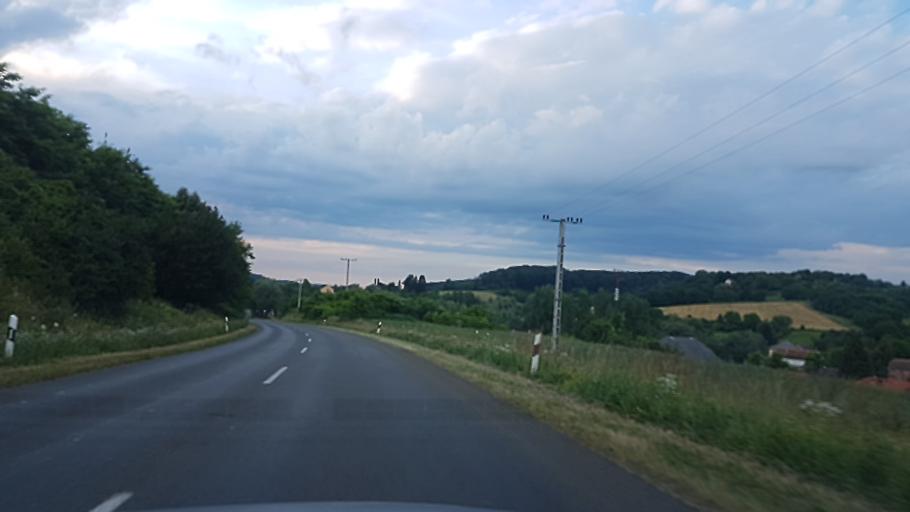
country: HU
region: Somogy
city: Kaposvar
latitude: 46.2812
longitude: 17.8208
